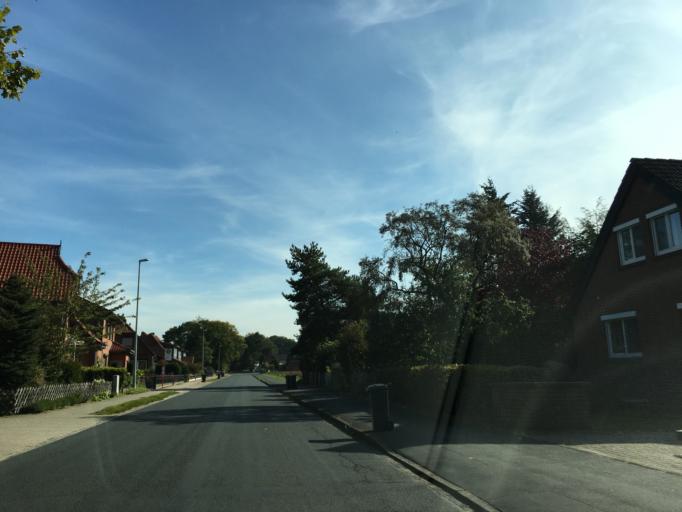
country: DE
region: Lower Saxony
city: Adendorf
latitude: 53.2769
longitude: 10.4710
